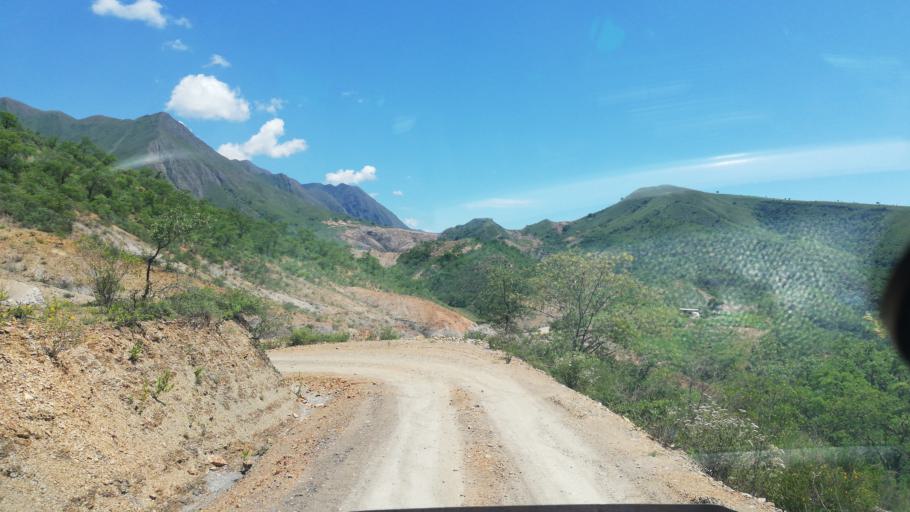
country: BO
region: Cochabamba
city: Mizque
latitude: -17.8430
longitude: -65.3075
